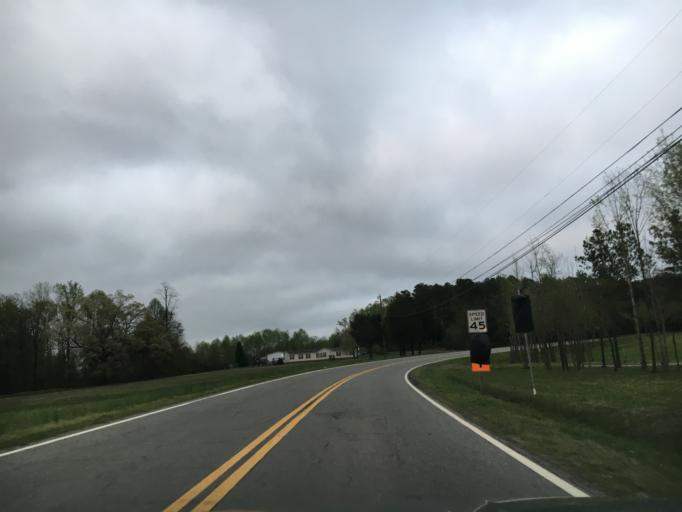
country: US
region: Virginia
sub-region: Halifax County
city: South Boston
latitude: 36.6815
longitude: -78.8974
